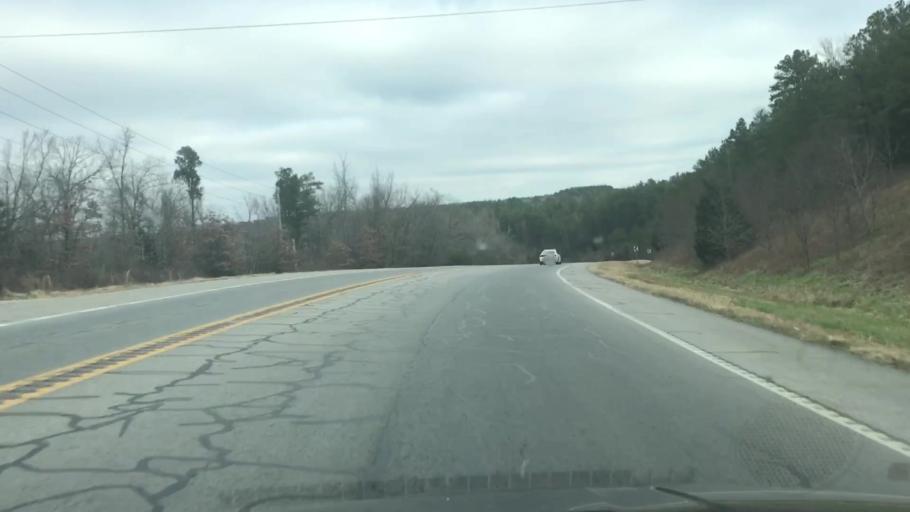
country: US
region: Arkansas
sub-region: Scott County
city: Waldron
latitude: 34.8203
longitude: -94.0371
